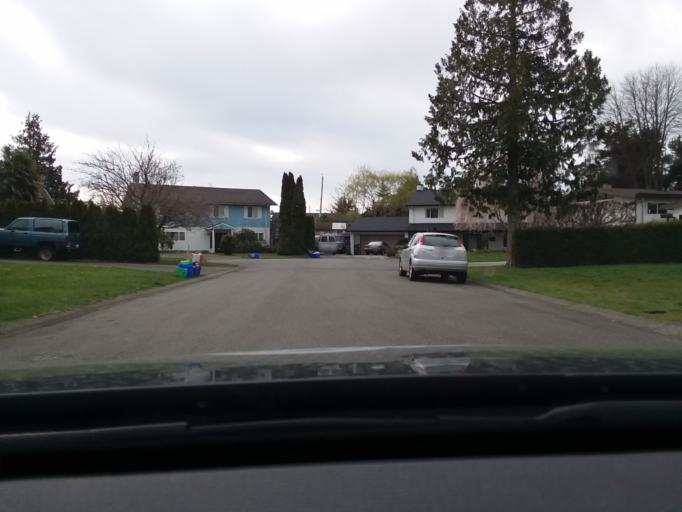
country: CA
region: British Columbia
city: Oak Bay
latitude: 48.4741
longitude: -123.3311
